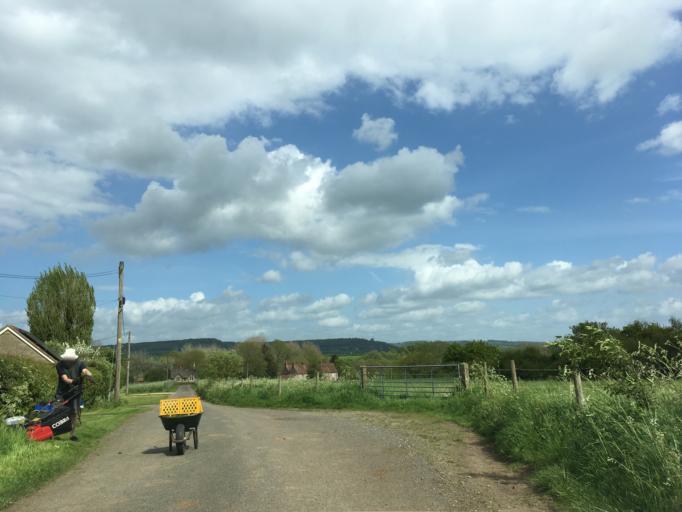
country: GB
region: England
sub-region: South Gloucestershire
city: Charfield
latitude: 51.6429
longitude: -2.4233
